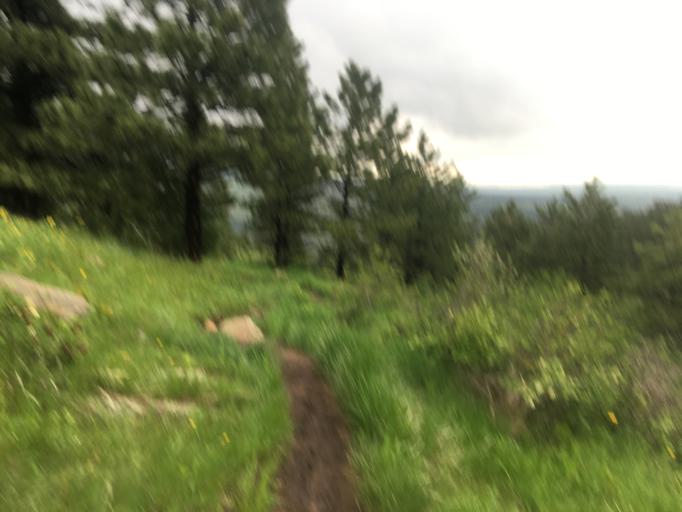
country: US
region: Colorado
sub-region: Boulder County
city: Boulder
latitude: 39.9211
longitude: -105.2767
